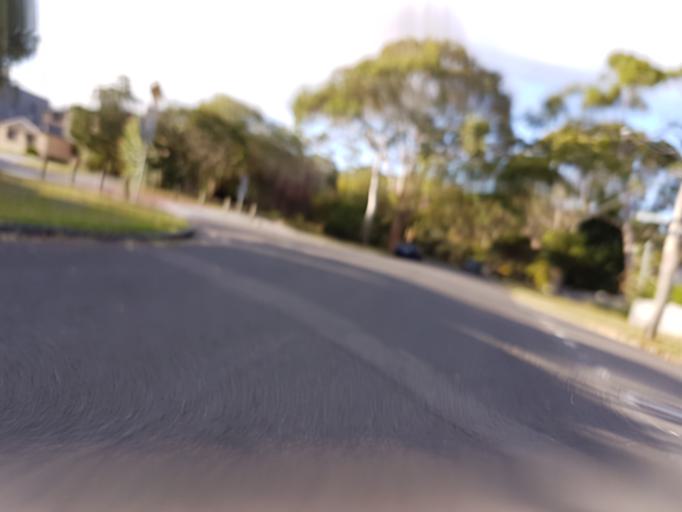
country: AU
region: New South Wales
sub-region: Manly Vale
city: Balgowlah
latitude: -33.7876
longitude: 151.2434
